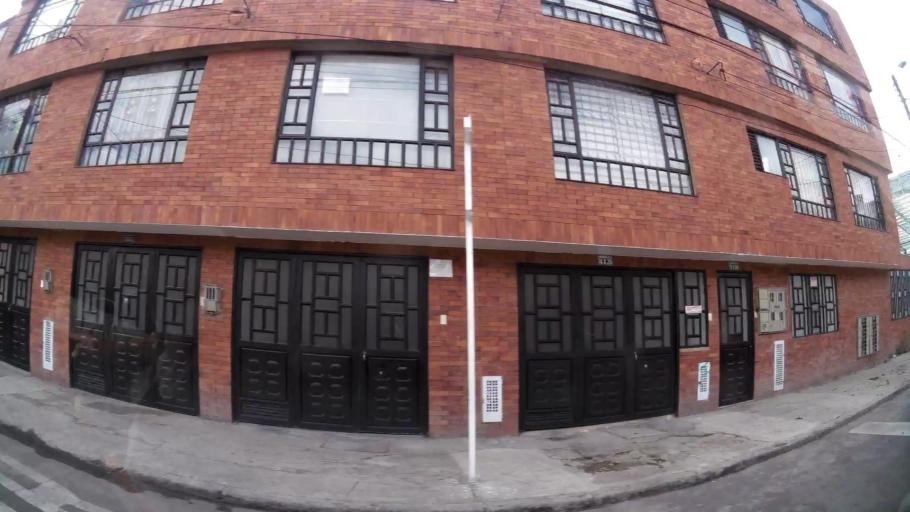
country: CO
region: Bogota D.C.
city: Barrio San Luis
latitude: 4.6965
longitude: -74.1006
